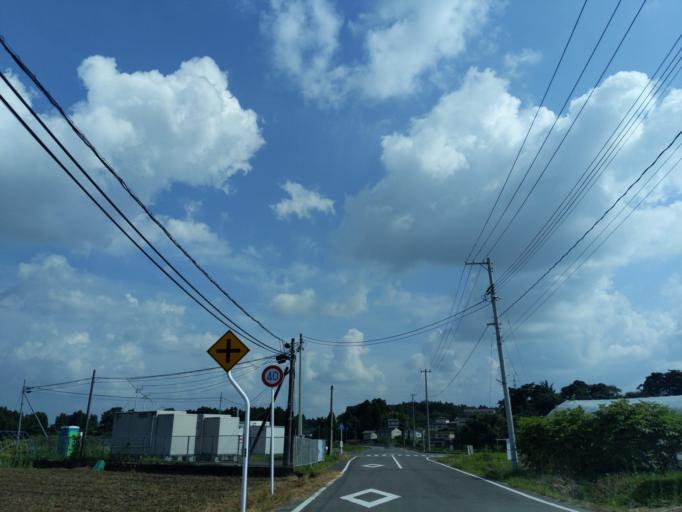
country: JP
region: Fukushima
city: Sukagawa
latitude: 37.3270
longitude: 140.3260
